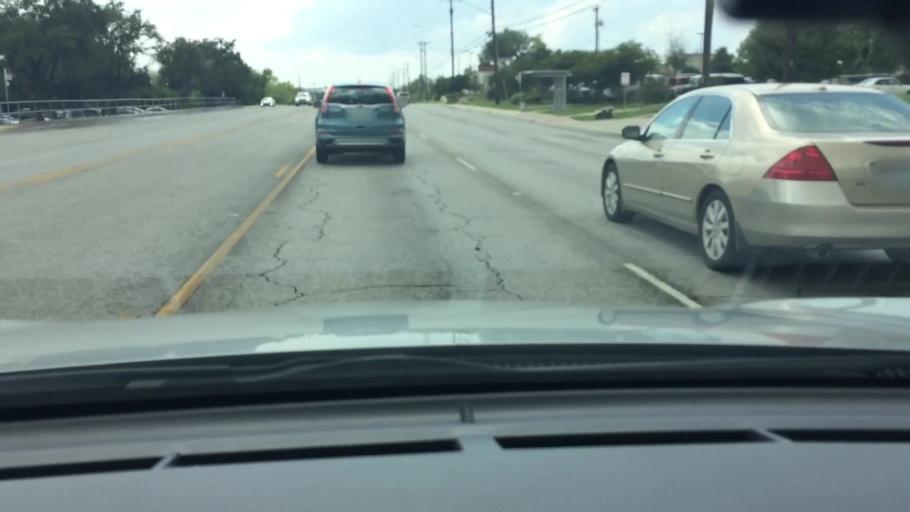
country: US
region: Texas
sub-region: Bexar County
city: Leon Valley
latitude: 29.5380
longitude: -98.5856
